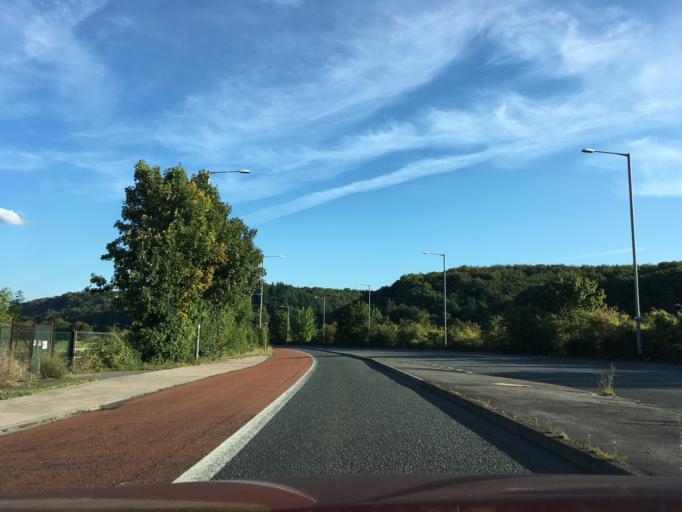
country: GB
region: England
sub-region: North Somerset
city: Long Ashton
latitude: 51.4753
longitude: -2.6486
